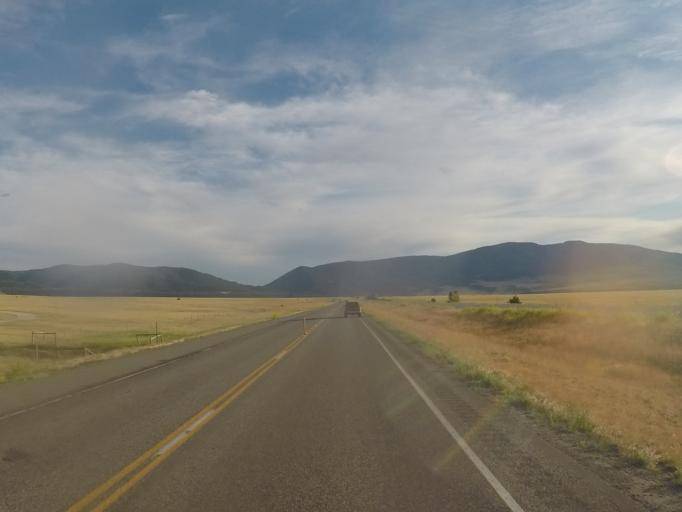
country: US
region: Montana
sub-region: Park County
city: Livingston
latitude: 45.6640
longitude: -110.5278
